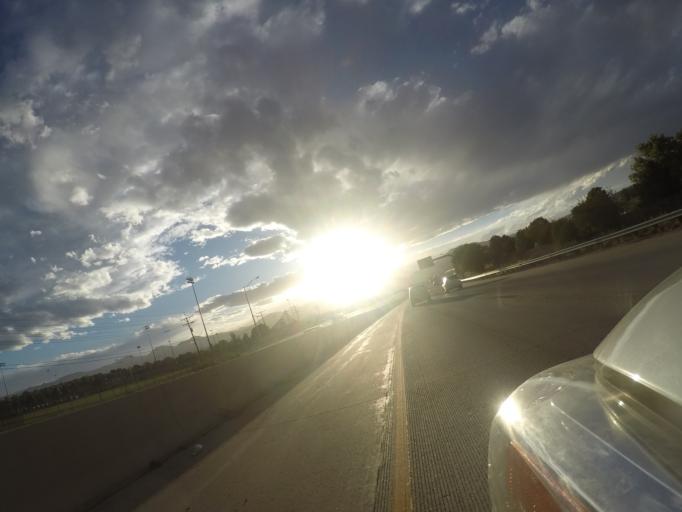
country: US
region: Colorado
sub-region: Jefferson County
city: Lakewood
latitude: 39.6535
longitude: -105.1047
